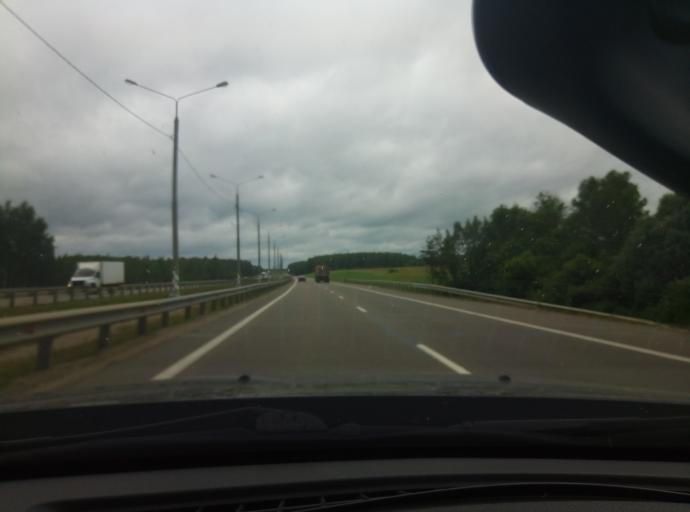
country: RU
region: Tula
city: Zaokskiy
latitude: 54.6769
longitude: 37.5058
